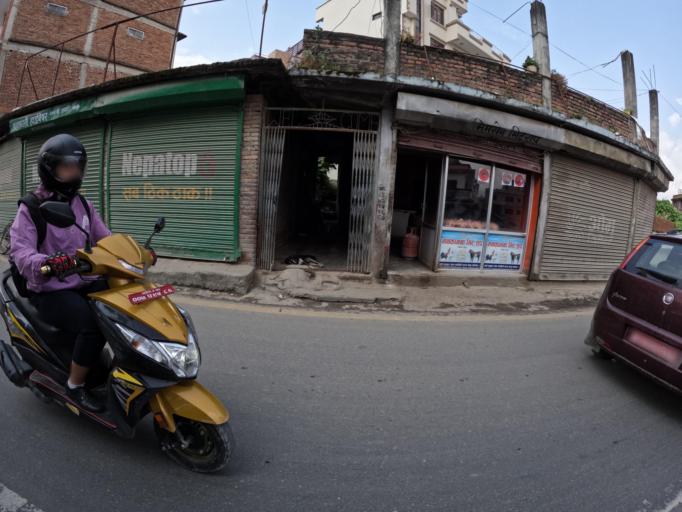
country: NP
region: Central Region
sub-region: Bagmati Zone
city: Patan
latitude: 27.6701
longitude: 85.3658
